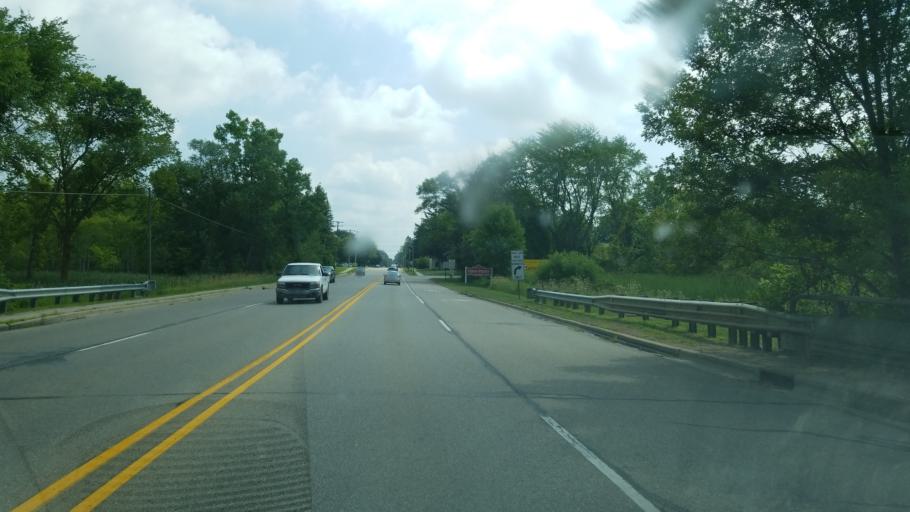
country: US
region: Michigan
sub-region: Kent County
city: Cedar Springs
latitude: 43.2199
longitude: -85.5629
